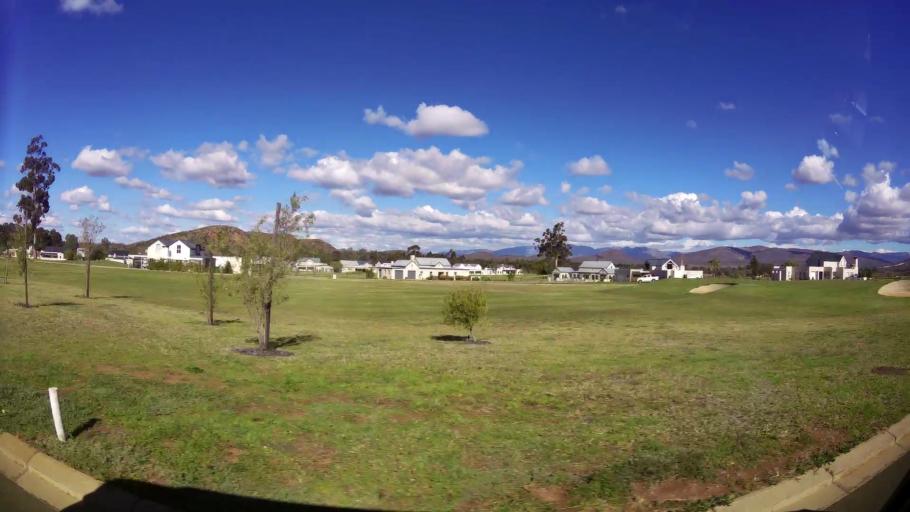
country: ZA
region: Western Cape
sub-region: Cape Winelands District Municipality
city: Ashton
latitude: -33.8137
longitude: 19.8459
